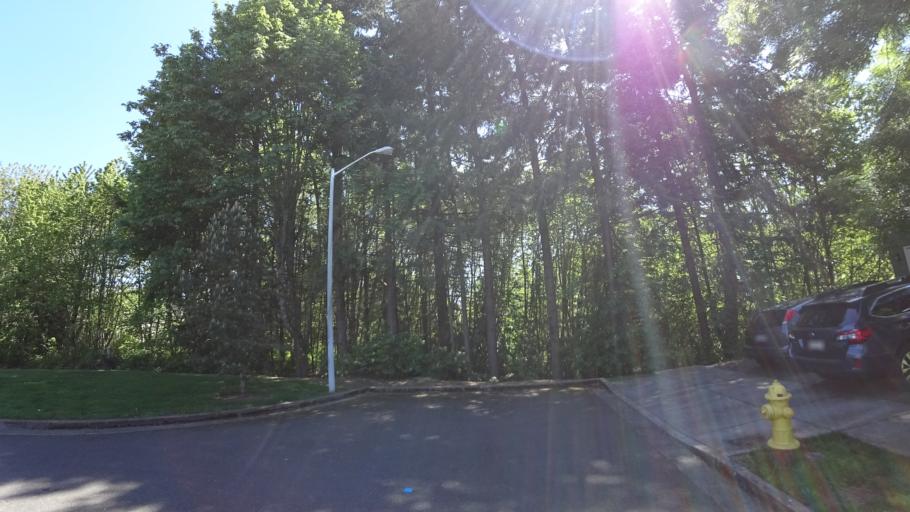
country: US
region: Oregon
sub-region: Washington County
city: Hillsboro
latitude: 45.5056
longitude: -122.9516
